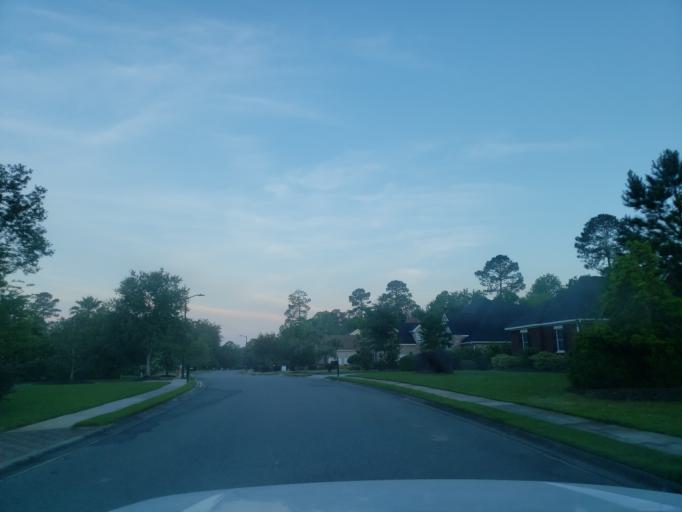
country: US
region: Georgia
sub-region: Chatham County
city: Pooler
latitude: 32.0704
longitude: -81.2408
